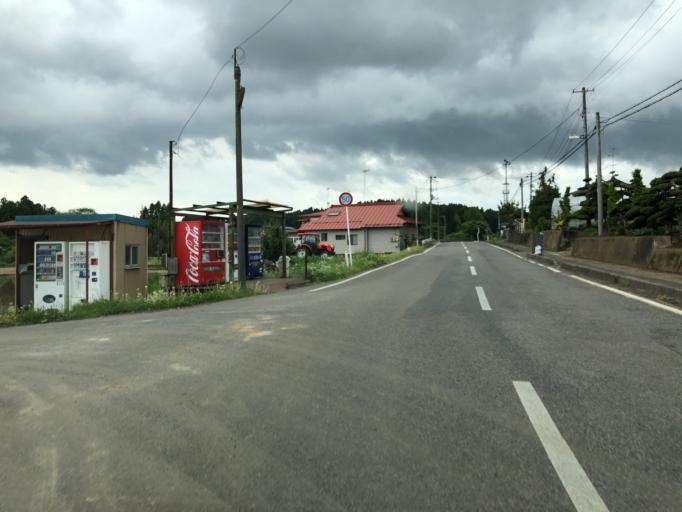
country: JP
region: Fukushima
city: Ishikawa
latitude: 37.1725
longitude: 140.4079
